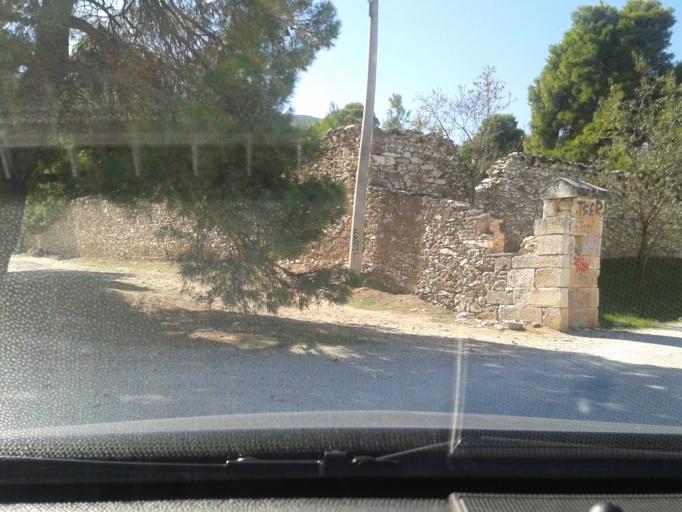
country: GR
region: Attica
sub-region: Nomarchia Anatolikis Attikis
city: Dionysos
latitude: 38.1005
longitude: 23.8843
